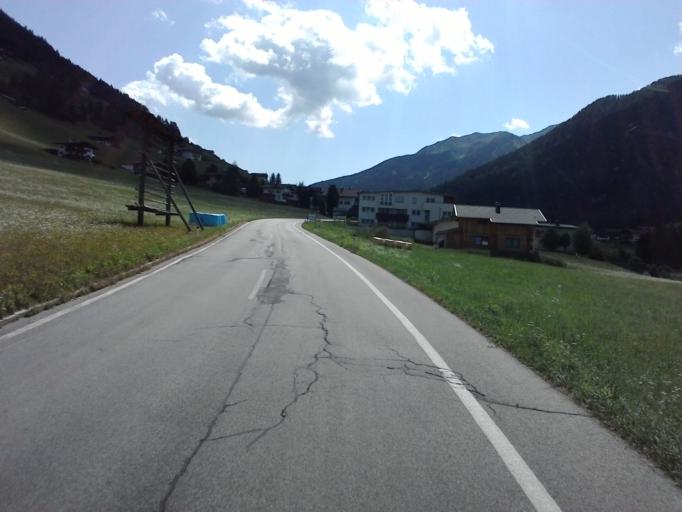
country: AT
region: Tyrol
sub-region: Politischer Bezirk Lienz
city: Kartitsch
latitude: 46.7282
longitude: 12.4928
